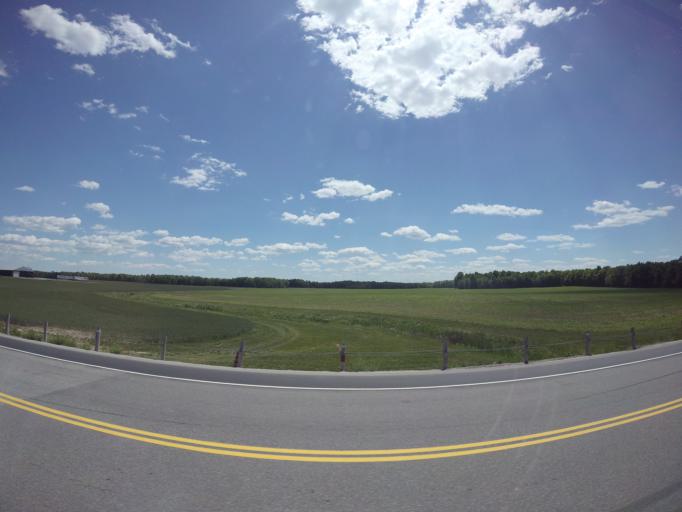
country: CA
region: Ontario
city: Carleton Place
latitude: 45.1334
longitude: -76.1959
